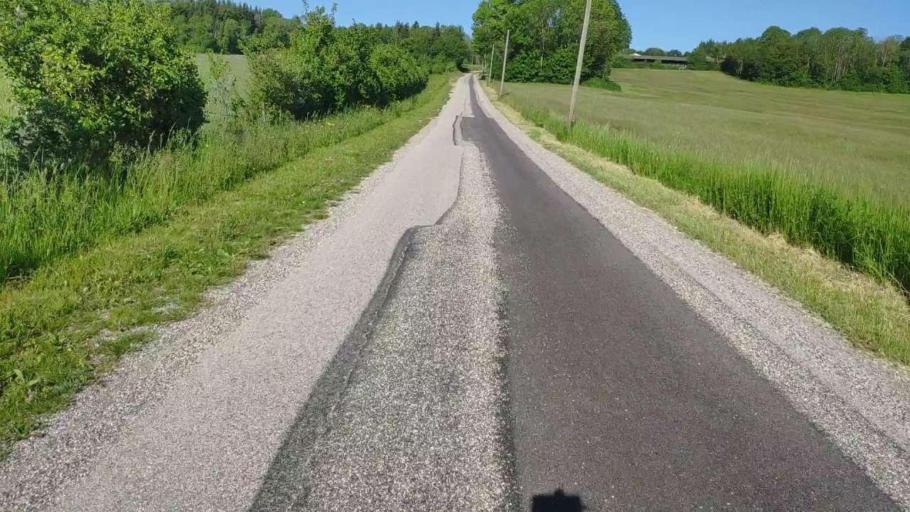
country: FR
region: Franche-Comte
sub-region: Departement du Jura
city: Perrigny
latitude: 46.6854
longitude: 5.6358
